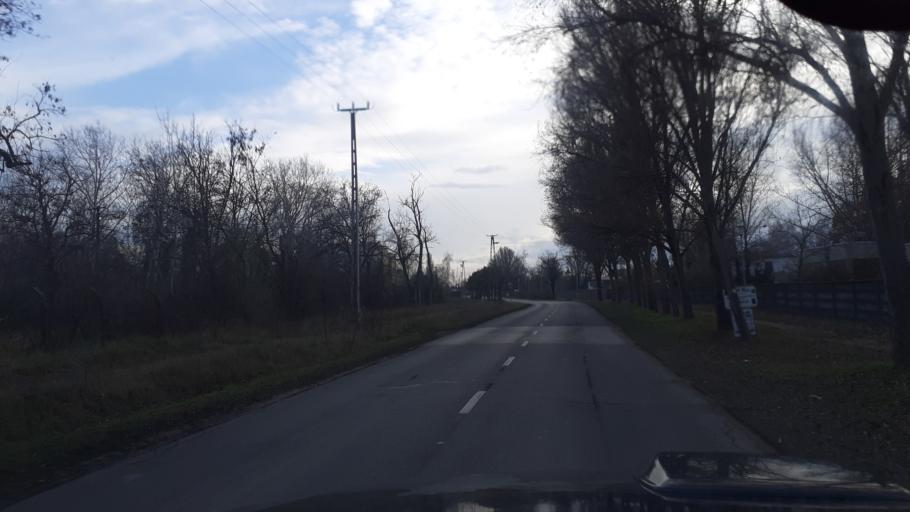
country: HU
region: Bacs-Kiskun
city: Szabadszallas
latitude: 46.8898
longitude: 19.2196
